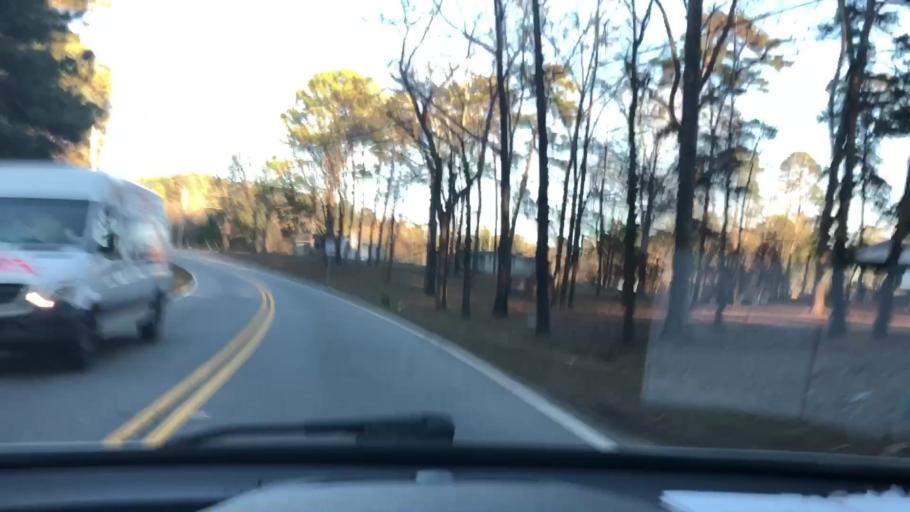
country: US
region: Georgia
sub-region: Rockdale County
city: Lakeview Estates
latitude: 33.7482
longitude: -84.0271
